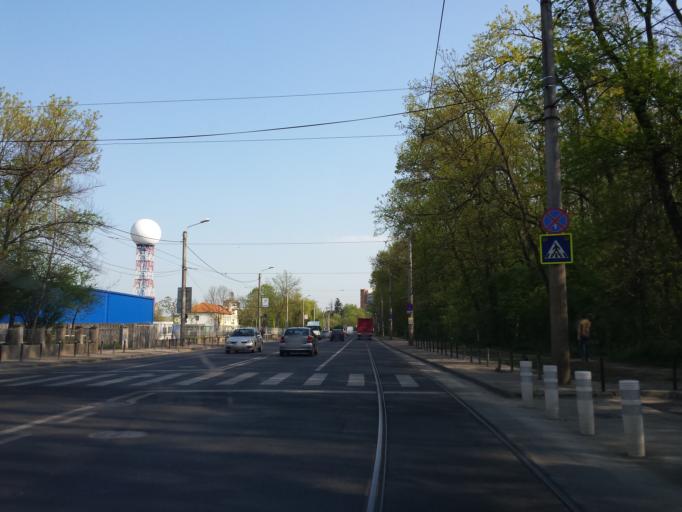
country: RO
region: Timis
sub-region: Comuna Dumbravita
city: Dumbravita
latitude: 45.7691
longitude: 21.2604
